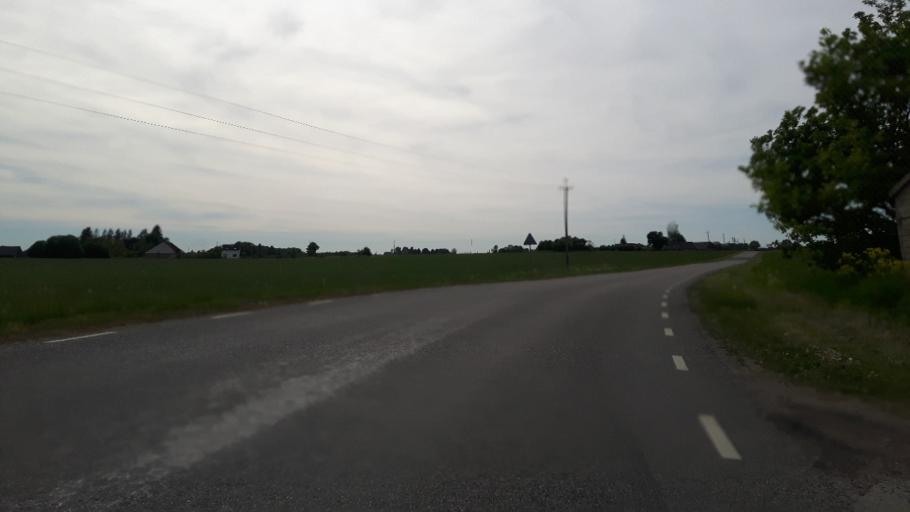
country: EE
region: Harju
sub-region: Maardu linn
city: Maardu
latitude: 59.4228
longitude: 25.0085
